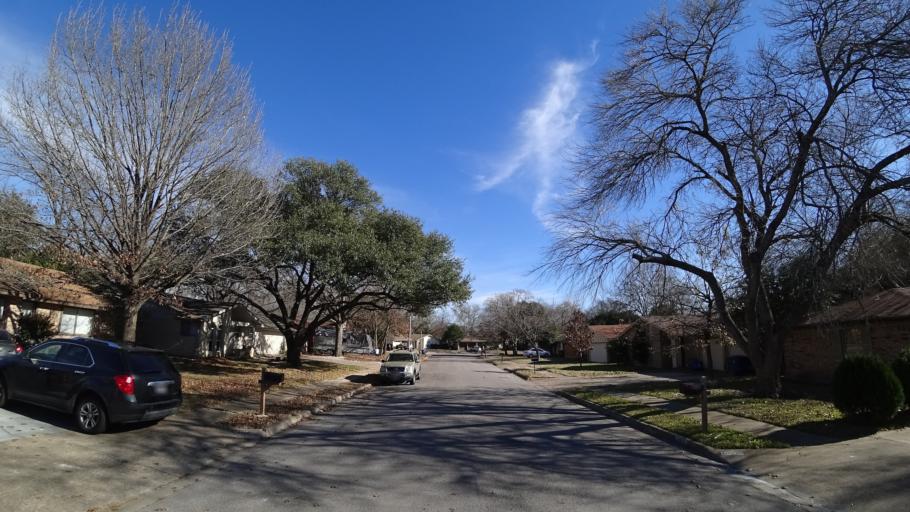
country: US
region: Texas
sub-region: Travis County
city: Wells Branch
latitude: 30.3809
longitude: -97.7061
